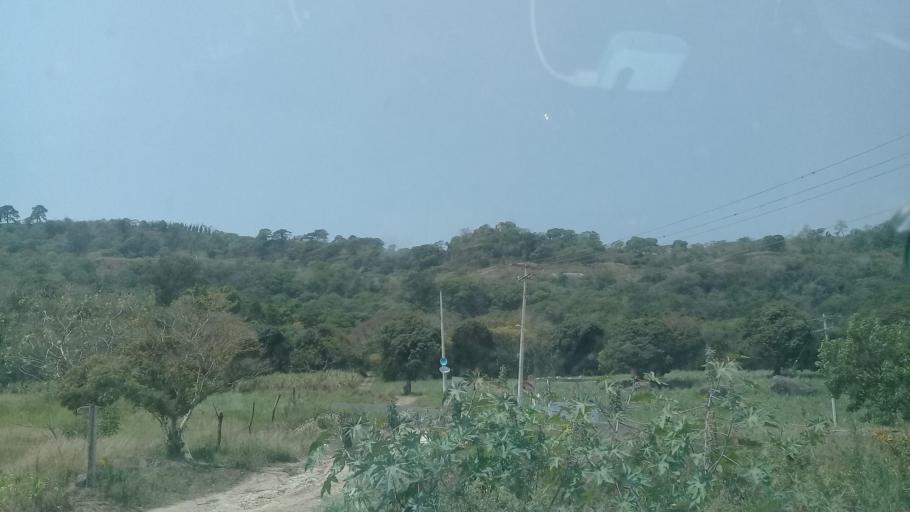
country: MX
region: Veracruz
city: El Castillo
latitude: 19.5664
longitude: -96.8451
